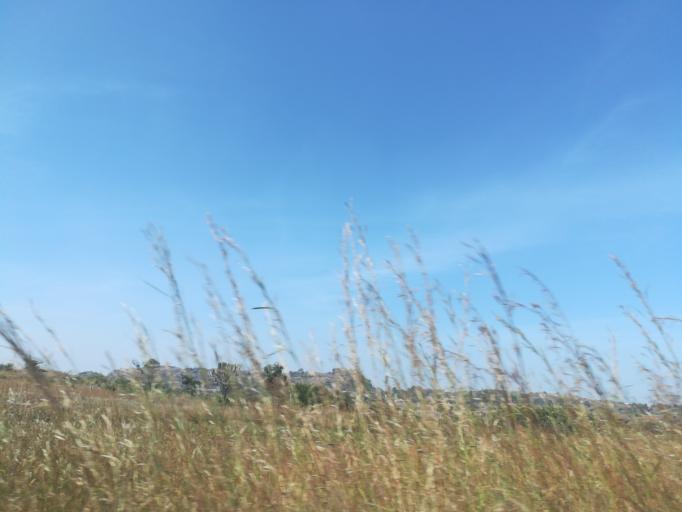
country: NG
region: Plateau
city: Bukuru
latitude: 9.7602
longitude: 8.9071
